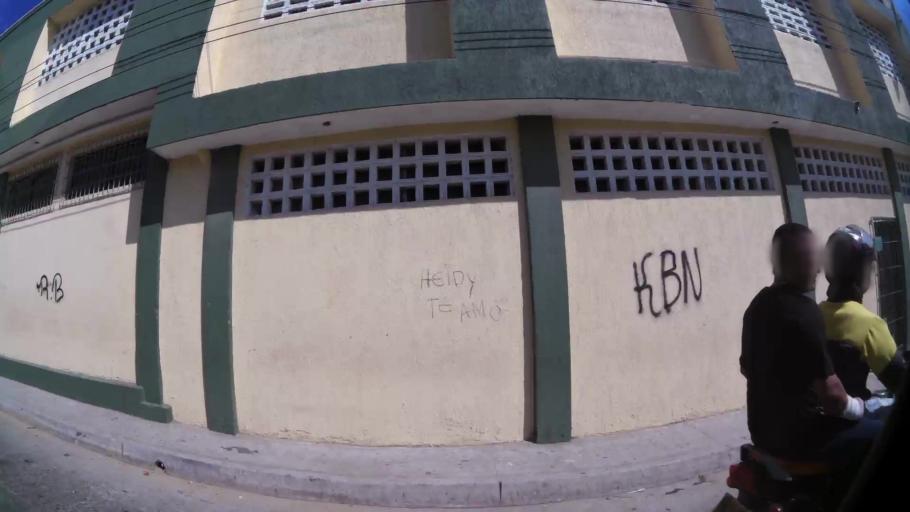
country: CO
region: Atlantico
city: Barranquilla
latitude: 10.9336
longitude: -74.8255
